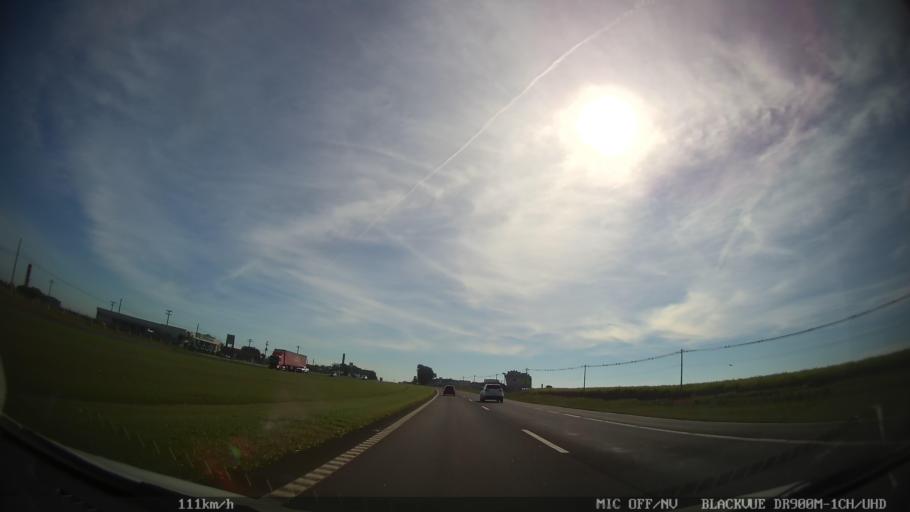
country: BR
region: Sao Paulo
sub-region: Araras
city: Araras
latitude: -22.4154
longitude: -47.3901
